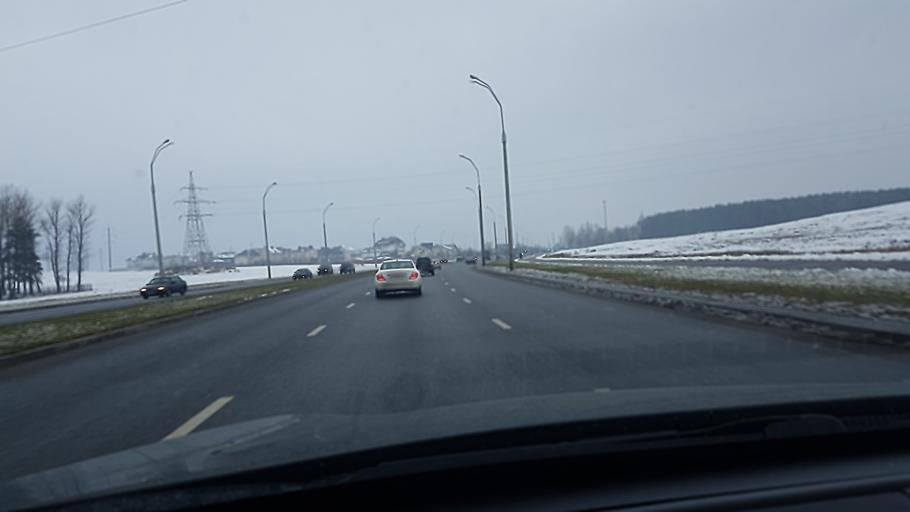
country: BY
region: Minsk
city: Minsk
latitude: 53.9479
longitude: 27.5370
